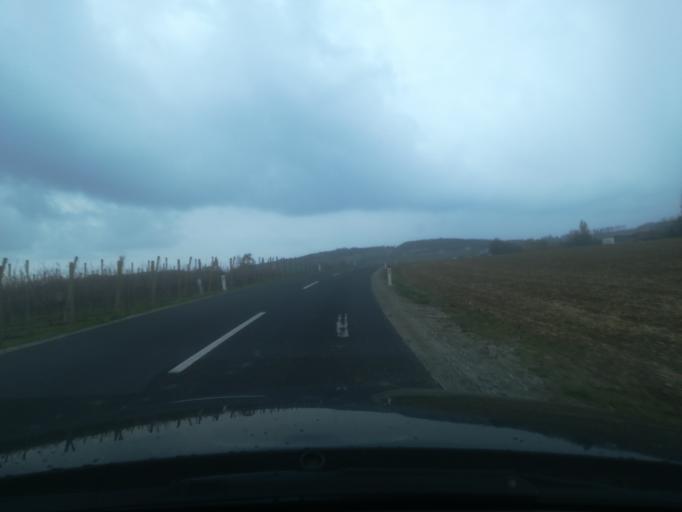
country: AT
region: Upper Austria
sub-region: Wels-Land
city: Holzhausen
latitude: 48.2283
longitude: 14.0703
